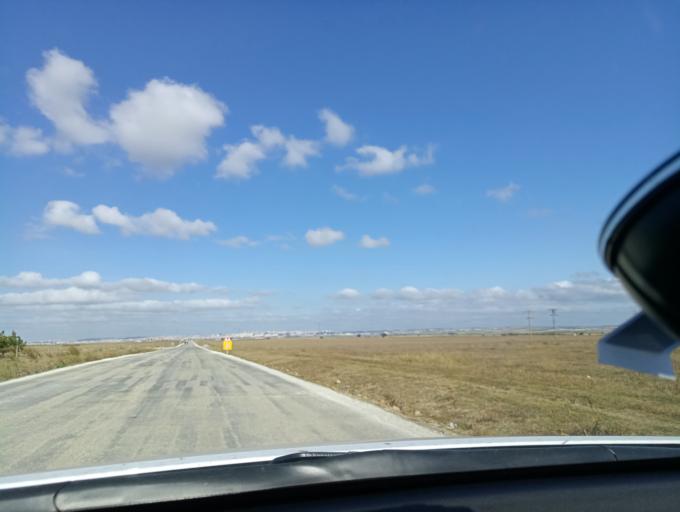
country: TR
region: Tekirdag
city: Corlu
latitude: 41.0655
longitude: 27.8339
